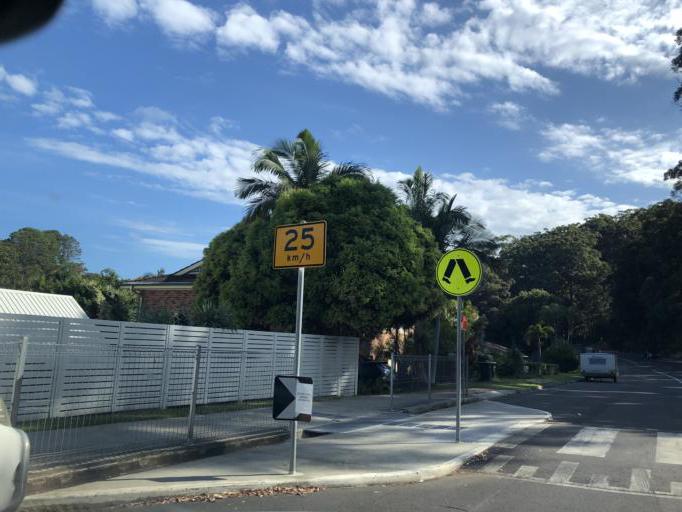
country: AU
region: New South Wales
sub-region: Coffs Harbour
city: Coffs Harbour
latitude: -30.2548
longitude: 153.1322
